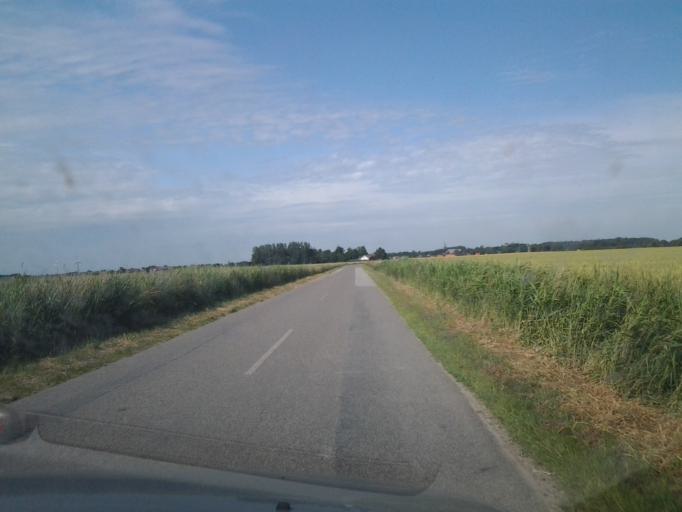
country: DE
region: Schleswig-Holstein
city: Aventoft
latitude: 54.9244
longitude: 8.7970
